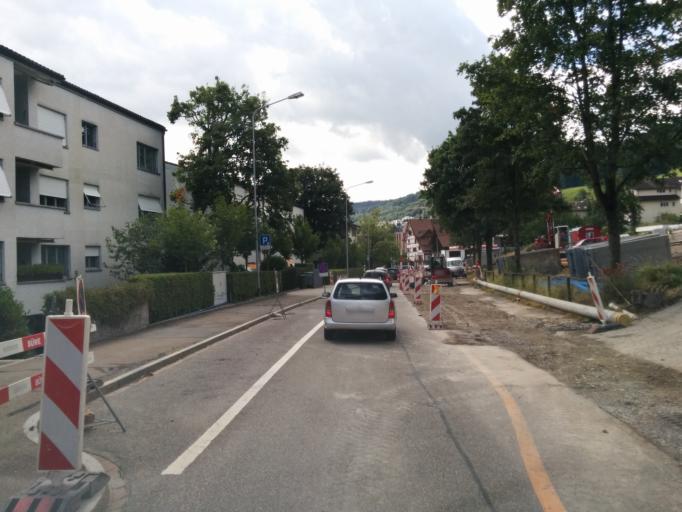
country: CH
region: Zurich
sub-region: Bezirk Horgen
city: Oberrieden / Mitte
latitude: 47.2727
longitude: 8.5805
